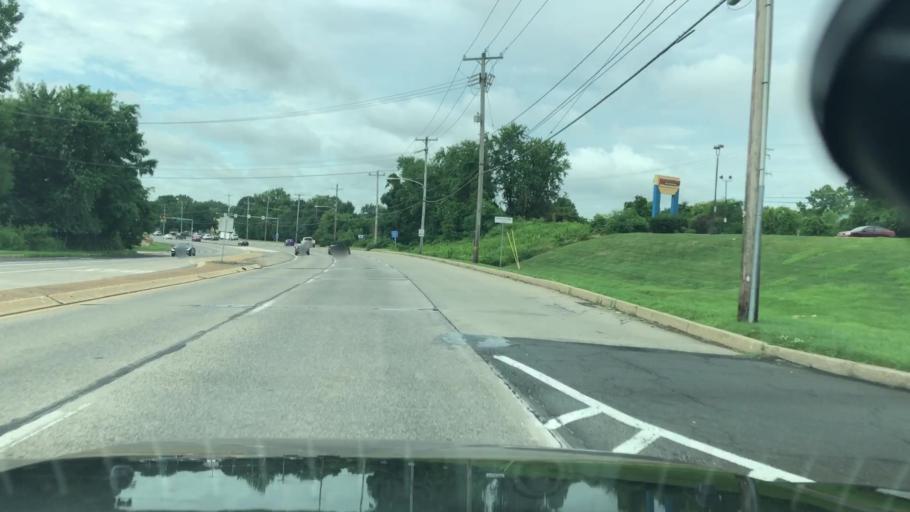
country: US
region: Pennsylvania
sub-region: Bucks County
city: Fairless Hills
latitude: 40.1856
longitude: -74.8696
